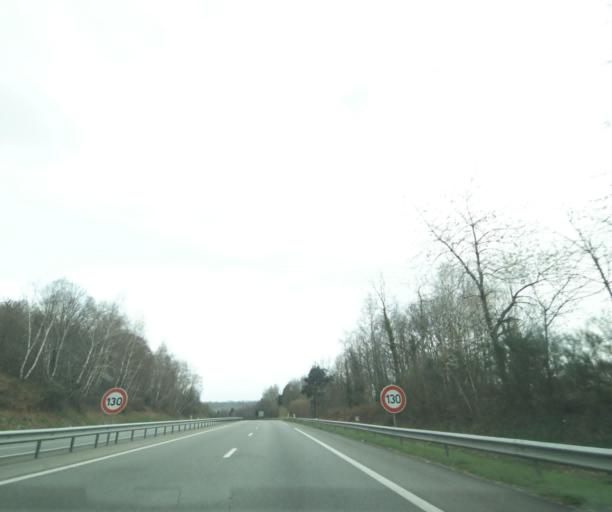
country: FR
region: Limousin
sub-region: Departement de la Haute-Vienne
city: Condat-sur-Vienne
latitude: 45.7760
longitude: 1.3077
